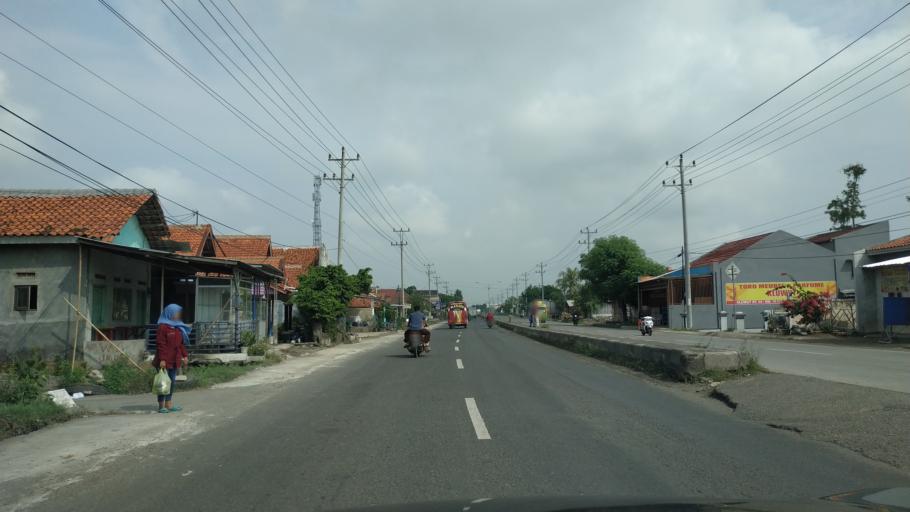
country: ID
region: Central Java
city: Bulakamba
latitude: -6.8742
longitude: 108.9154
